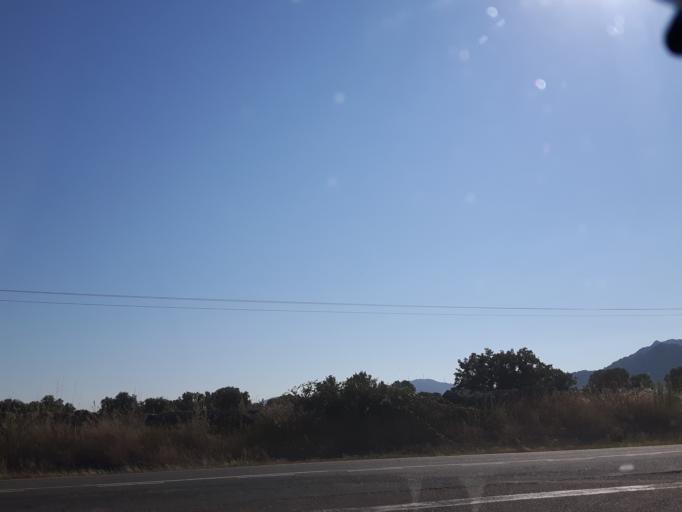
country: ES
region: Castille and Leon
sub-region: Provincia de Salamanca
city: Valdehijaderos
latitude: 40.4303
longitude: -5.8224
